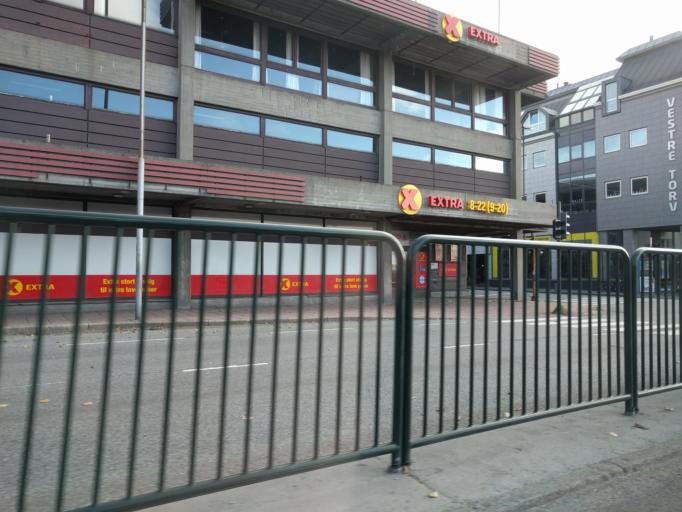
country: NO
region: Vest-Agder
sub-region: Kristiansand
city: Kristiansand
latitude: 58.1460
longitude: 7.9887
